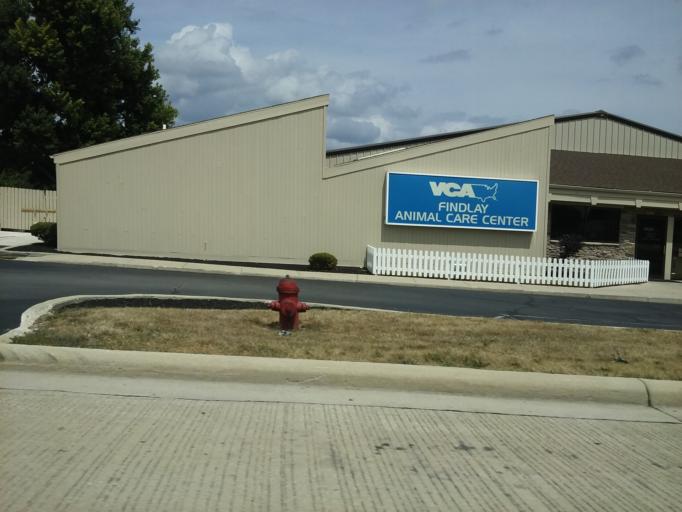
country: US
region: Ohio
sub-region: Hancock County
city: Findlay
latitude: 41.0422
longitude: -83.6764
